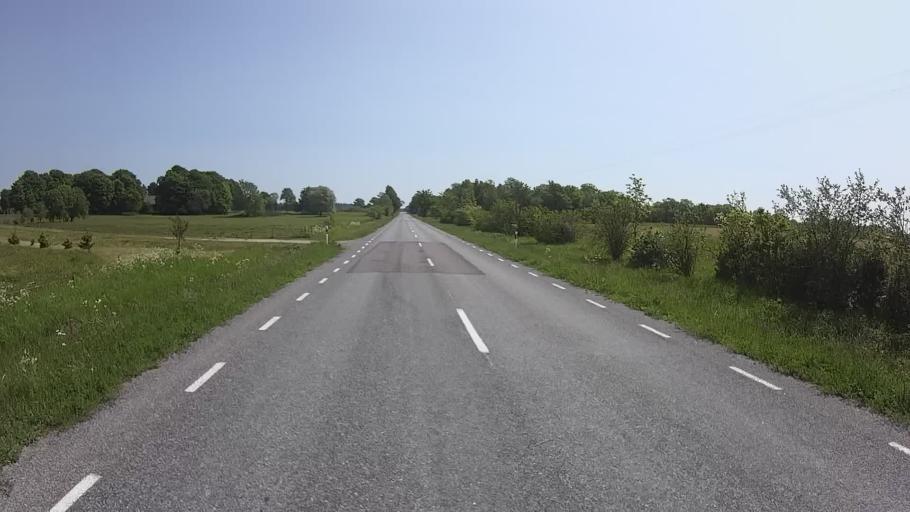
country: EE
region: Saare
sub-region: Kuressaare linn
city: Kuressaare
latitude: 58.3691
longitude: 22.0486
